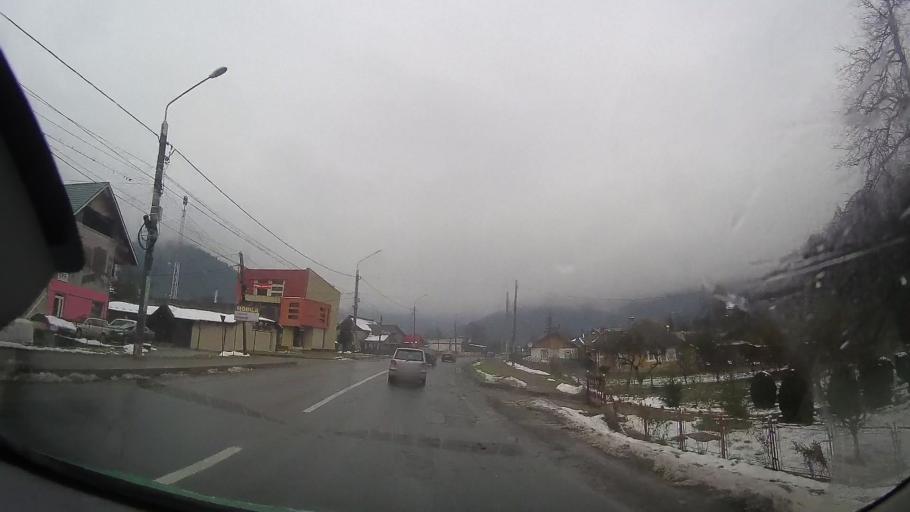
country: RO
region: Neamt
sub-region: Comuna Bicaz
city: Dodeni
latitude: 46.9041
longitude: 26.1100
